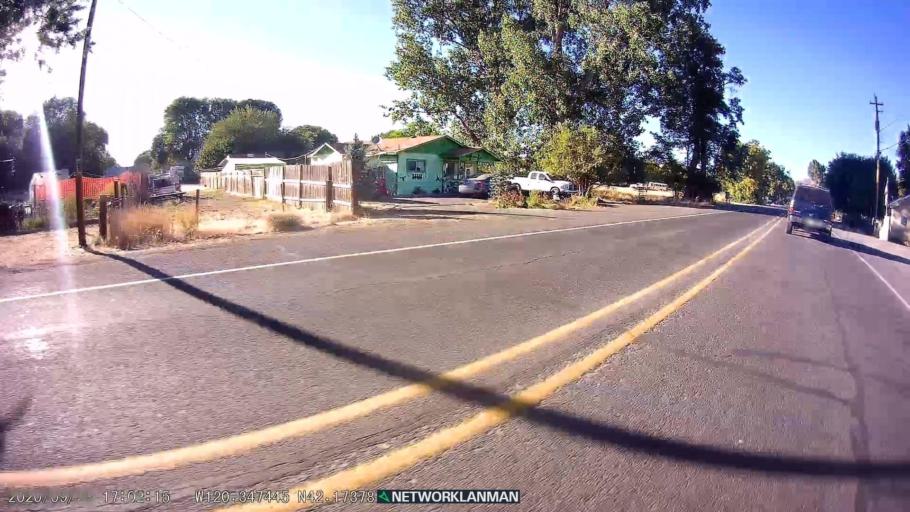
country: US
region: Oregon
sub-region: Lake County
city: Lakeview
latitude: 42.1741
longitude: -120.3474
